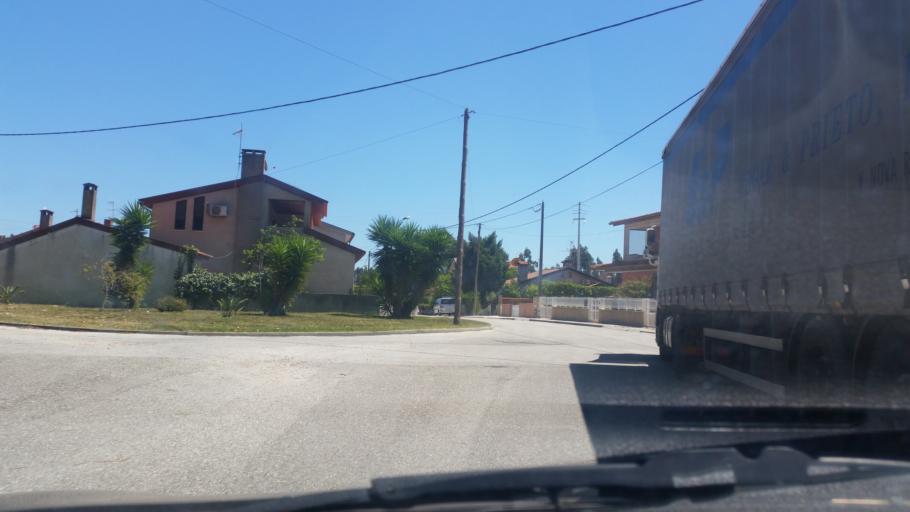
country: PT
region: Aveiro
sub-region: Agueda
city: Valongo
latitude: 40.5942
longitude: -8.4946
